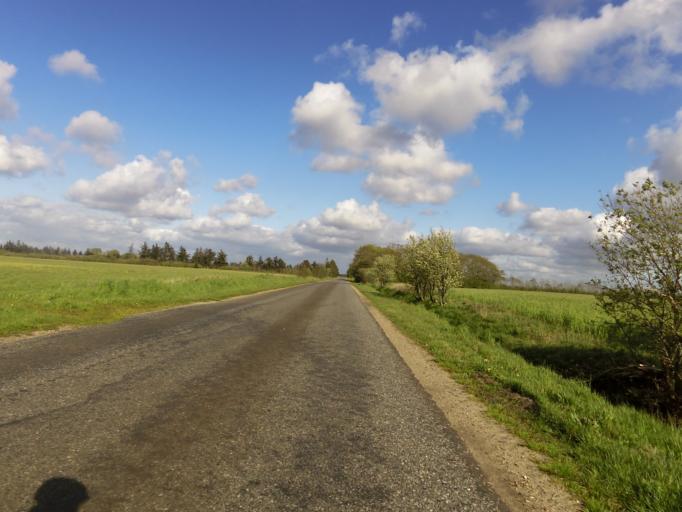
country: DK
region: South Denmark
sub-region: Esbjerg Kommune
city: Ribe
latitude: 55.2610
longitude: 8.7707
